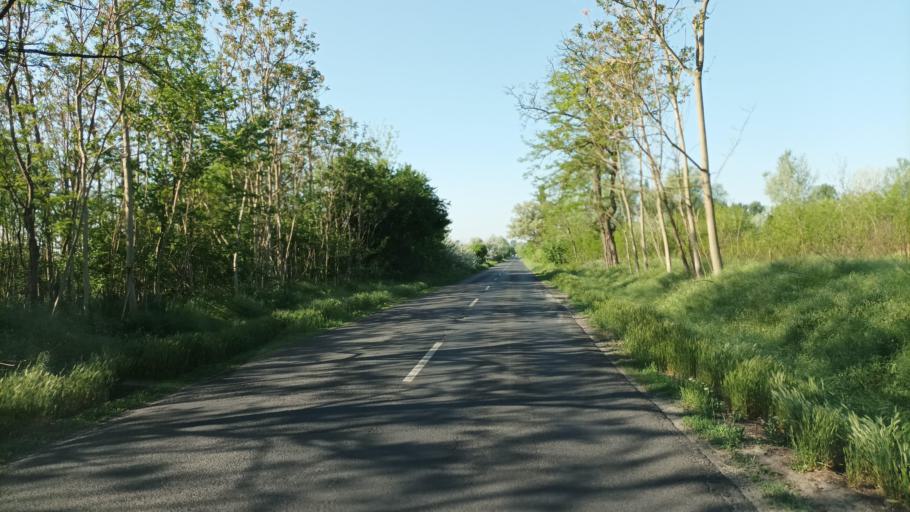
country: HU
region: Pest
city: Monor
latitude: 47.3135
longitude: 19.4445
